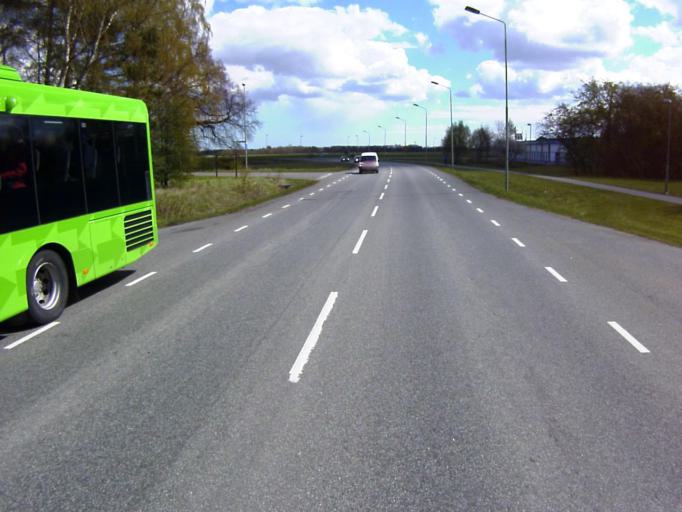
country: SE
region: Skane
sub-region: Kristianstads Kommun
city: Kristianstad
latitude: 56.0157
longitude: 14.1215
